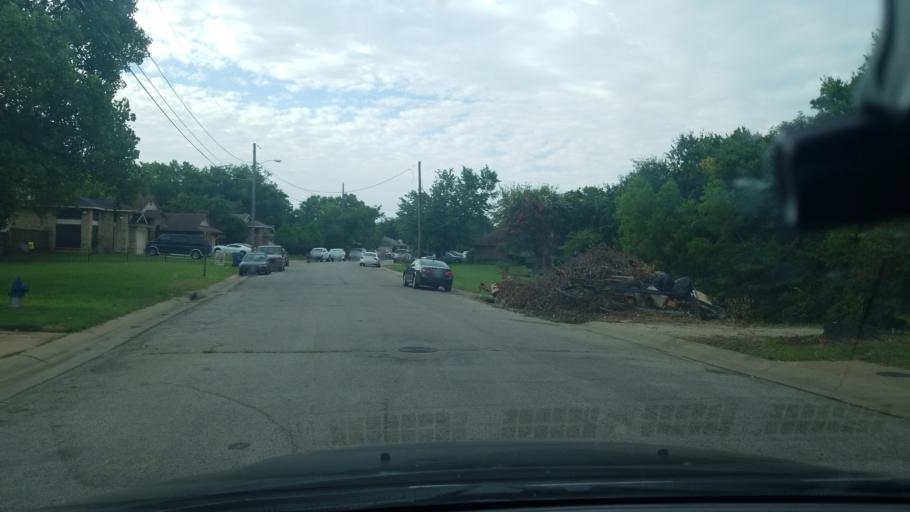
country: US
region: Texas
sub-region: Dallas County
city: Balch Springs
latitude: 32.7382
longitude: -96.6623
